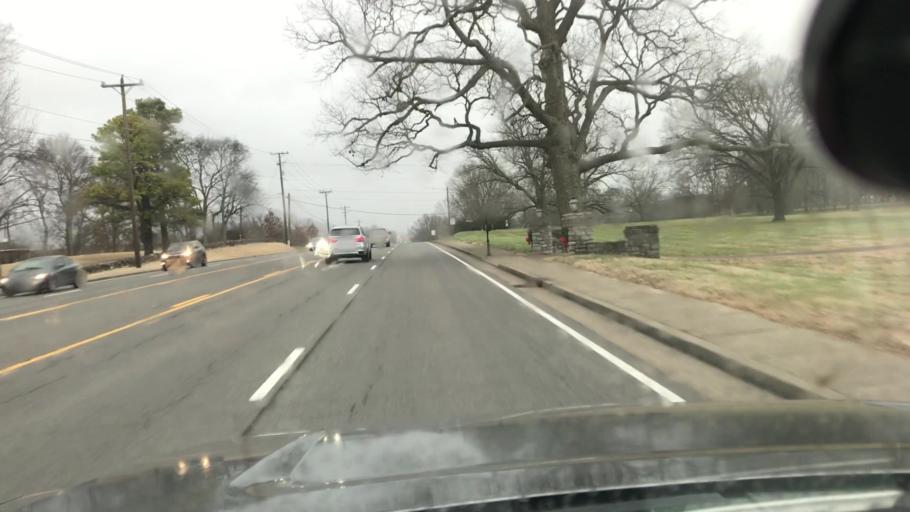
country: US
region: Tennessee
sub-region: Williamson County
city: Brentwood Estates
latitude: 36.0207
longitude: -86.7957
